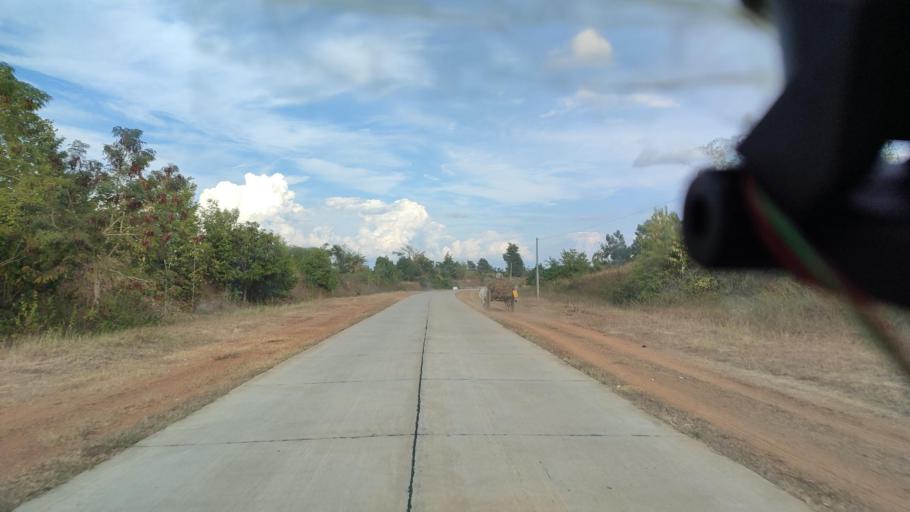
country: MM
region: Mandalay
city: Yamethin
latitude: 20.0959
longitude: 95.9723
